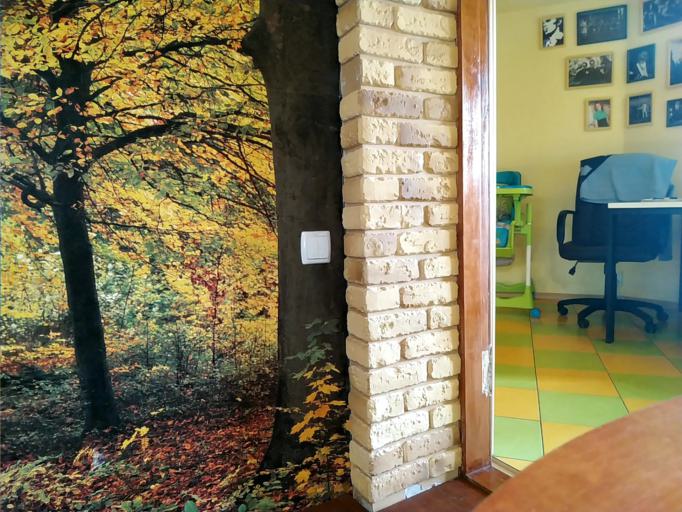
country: RU
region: Jaroslavl
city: Krasnyy Profintern
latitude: 58.0425
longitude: 40.4516
